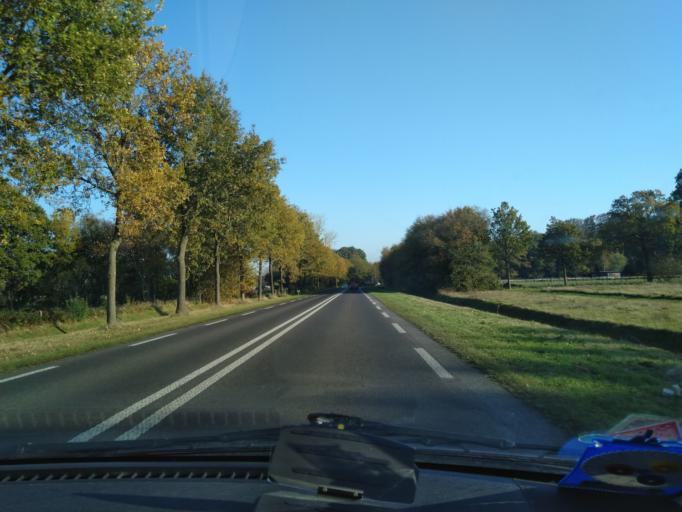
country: NL
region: Drenthe
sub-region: Gemeente Tynaarlo
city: Vries
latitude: 53.0803
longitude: 6.5843
